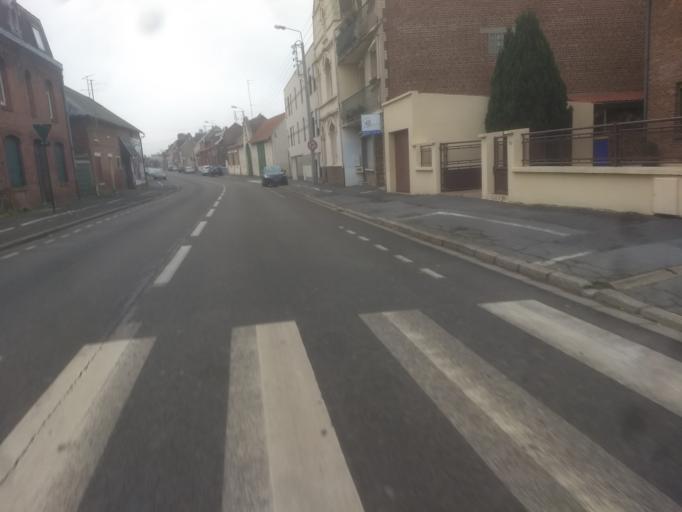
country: FR
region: Nord-Pas-de-Calais
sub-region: Departement du Pas-de-Calais
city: Saint-Laurent-Blangy
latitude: 50.3035
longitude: 2.8104
